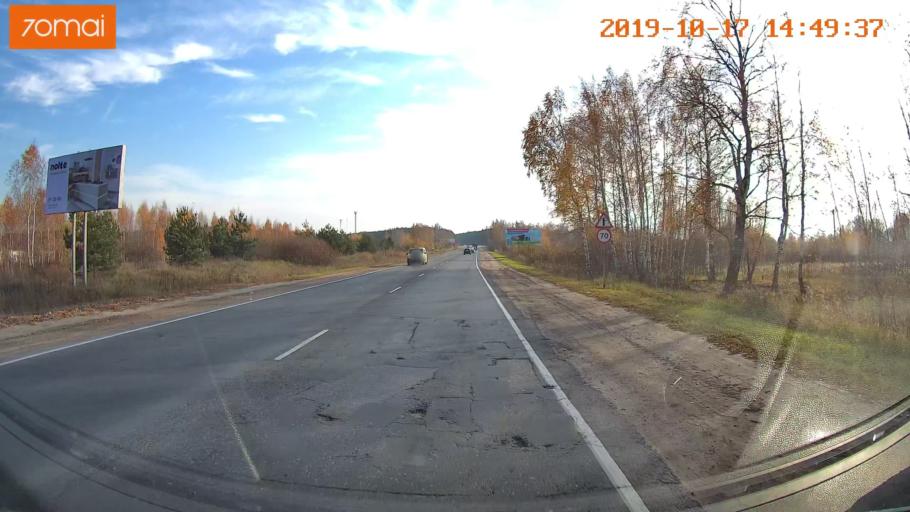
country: RU
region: Rjazan
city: Polyany
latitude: 54.7446
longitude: 39.8403
